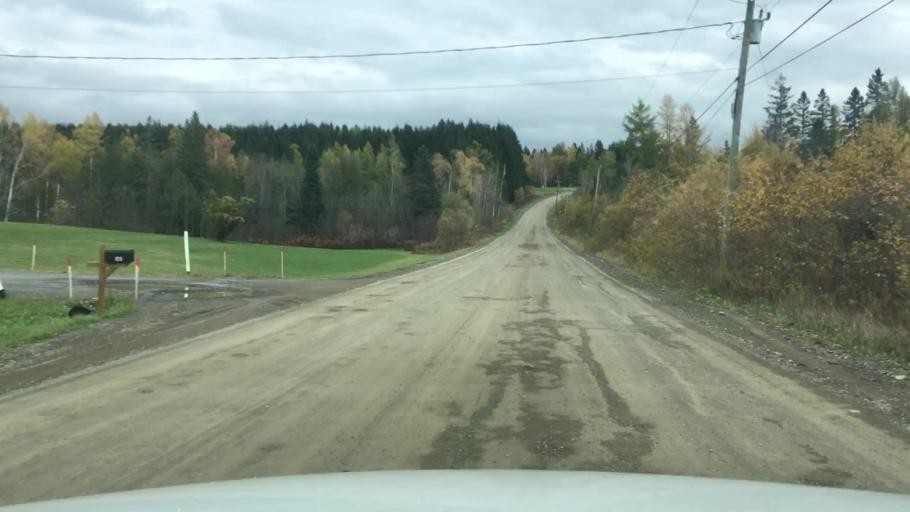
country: US
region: Maine
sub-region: Aroostook County
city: Easton
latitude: 46.5225
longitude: -67.8918
